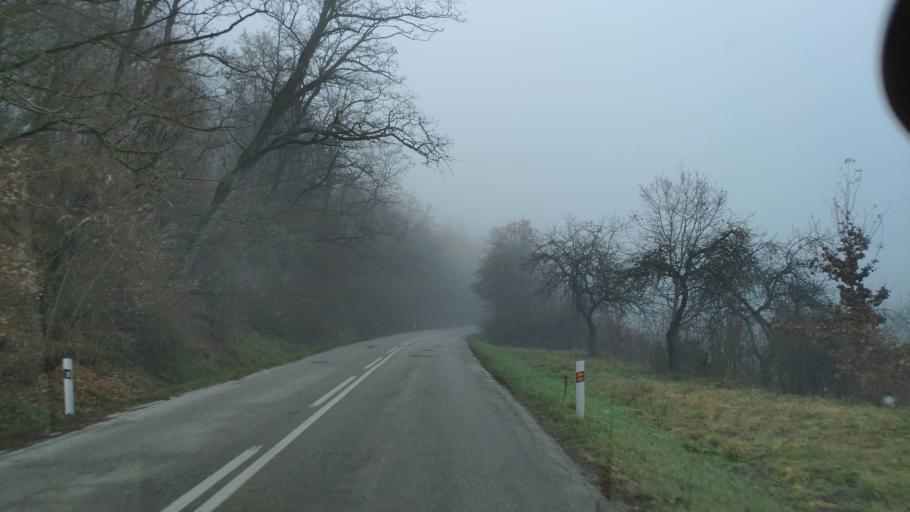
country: SK
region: Kosicky
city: Roznava
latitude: 48.6359
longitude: 20.3559
